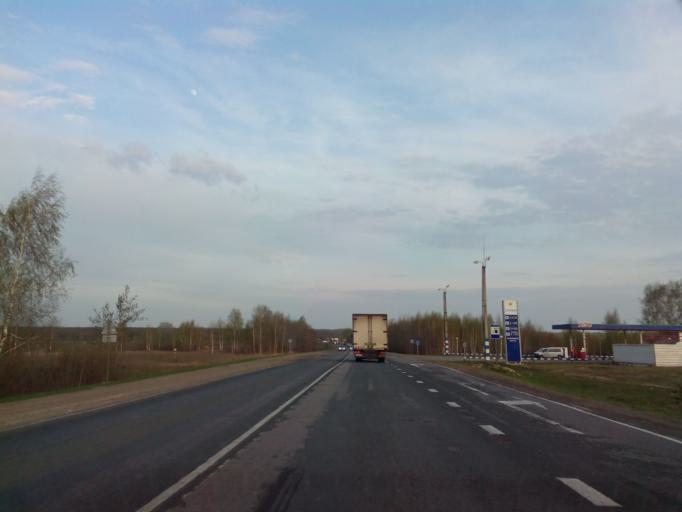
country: RU
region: Rjazan
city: Ryazhsk
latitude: 53.7217
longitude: 39.9121
